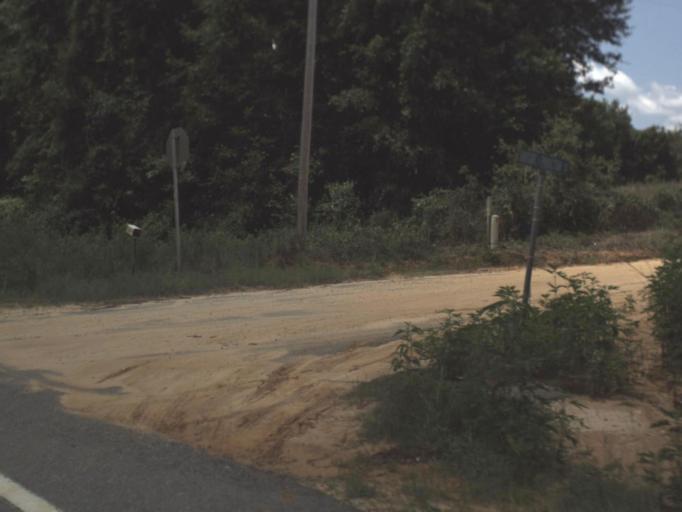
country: US
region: Florida
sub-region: Jefferson County
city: Monticello
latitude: 30.5638
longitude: -83.6374
